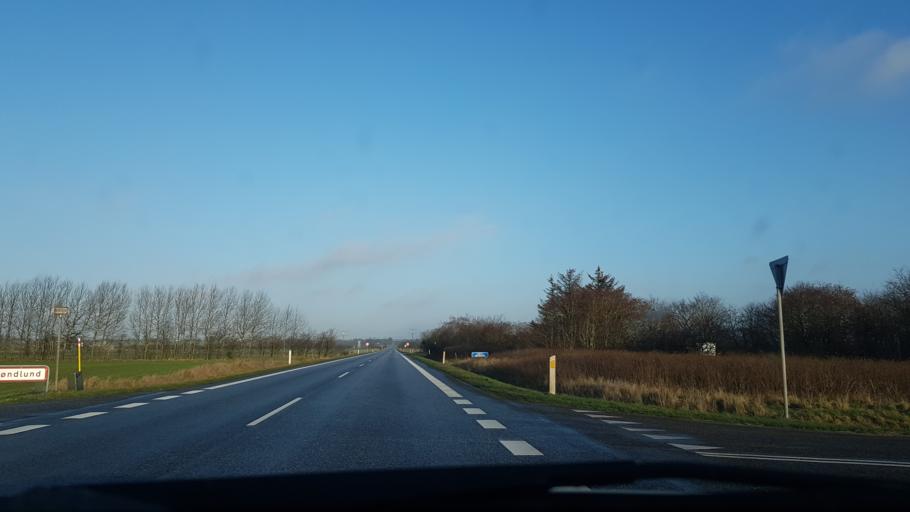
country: DK
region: South Denmark
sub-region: Tonder Kommune
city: Toftlund
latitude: 55.2358
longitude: 9.1249
